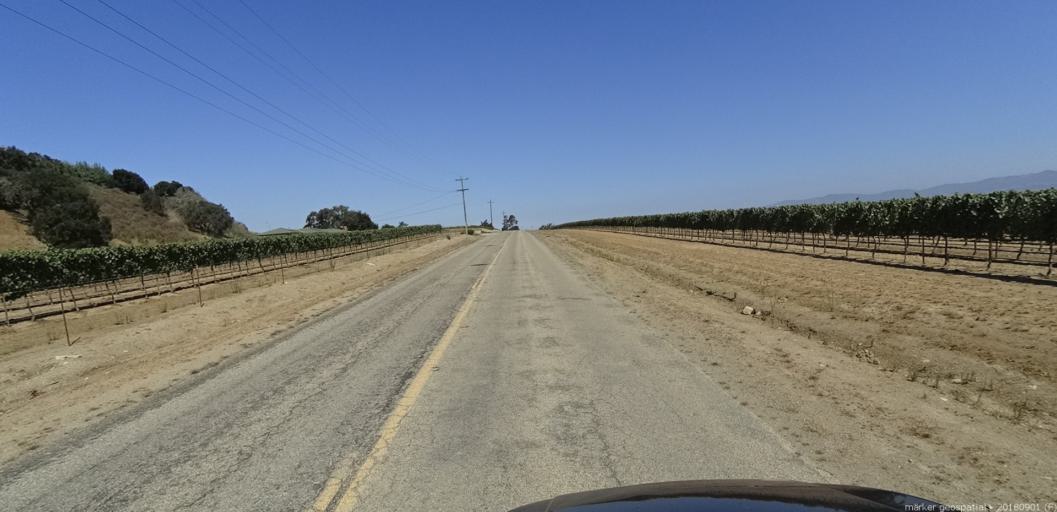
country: US
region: California
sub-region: Monterey County
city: Chualar
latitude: 36.5167
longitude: -121.5193
